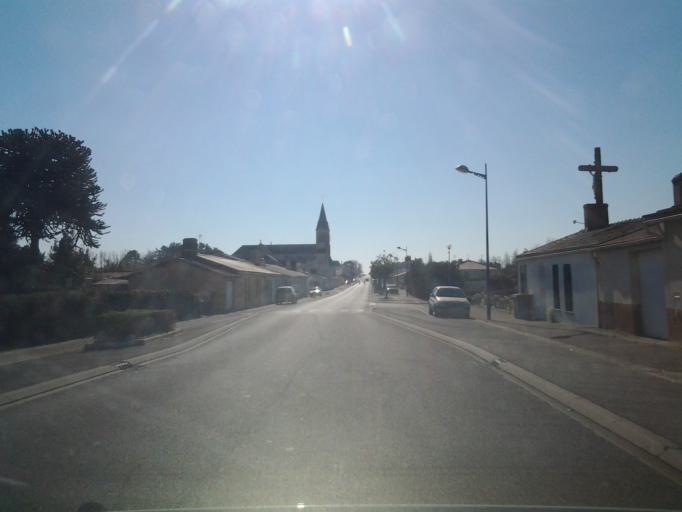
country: FR
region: Pays de la Loire
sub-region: Departement de la Vendee
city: Saint-Mathurin
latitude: 46.5672
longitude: -1.7121
